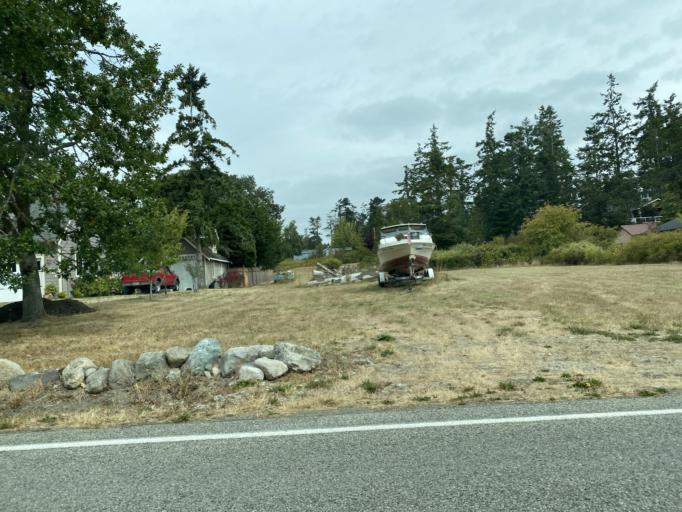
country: US
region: Washington
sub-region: Island County
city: Coupeville
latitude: 48.2395
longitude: -122.7055
